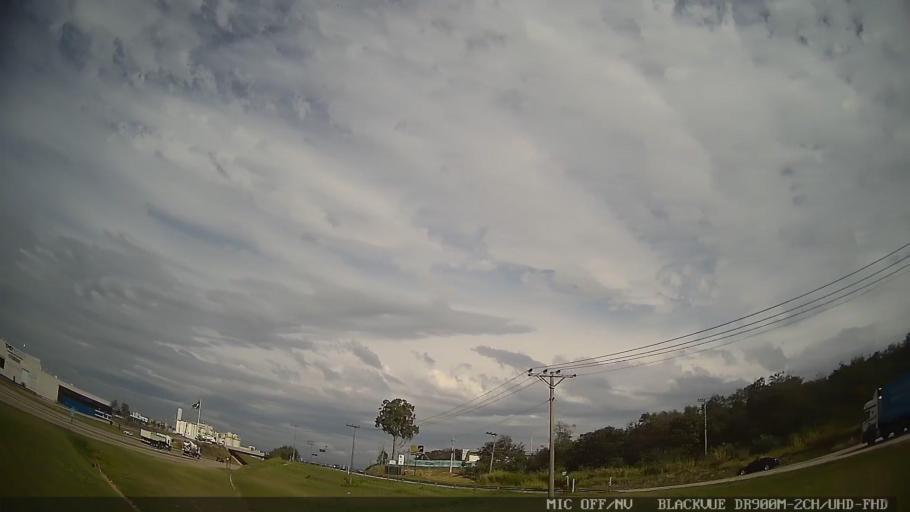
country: BR
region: Sao Paulo
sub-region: Salto
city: Salto
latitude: -23.1691
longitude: -47.2684
